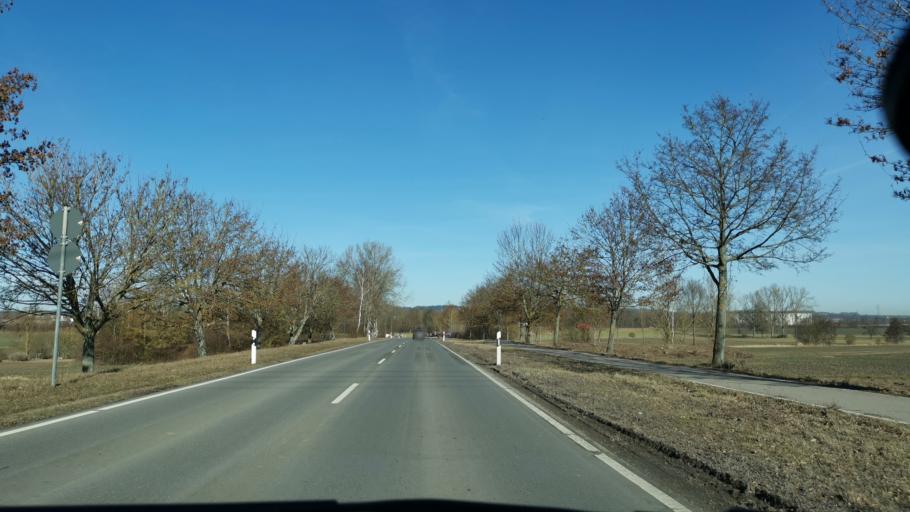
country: DE
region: Baden-Wuerttemberg
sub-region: Regierungsbezirk Stuttgart
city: Gartringen
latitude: 48.6284
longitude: 8.9205
